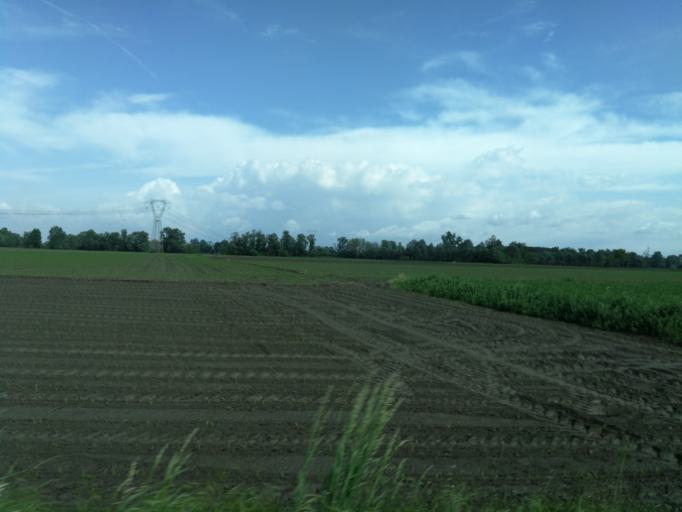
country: IT
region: Piedmont
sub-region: Provincia di Torino
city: Pancalieri
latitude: 44.8200
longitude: 7.5862
